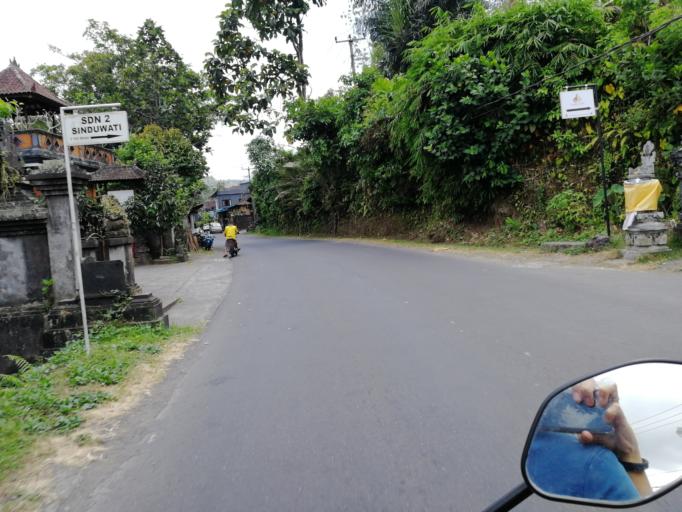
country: ID
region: Bali
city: Banjar Wangsian
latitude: -8.4619
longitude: 115.4492
